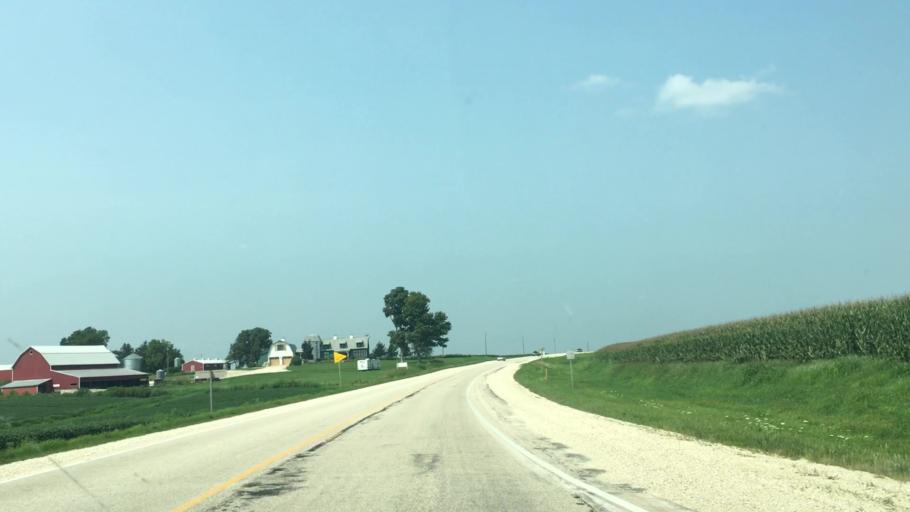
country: US
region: Iowa
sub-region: Fayette County
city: West Union
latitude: 42.9793
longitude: -91.8235
